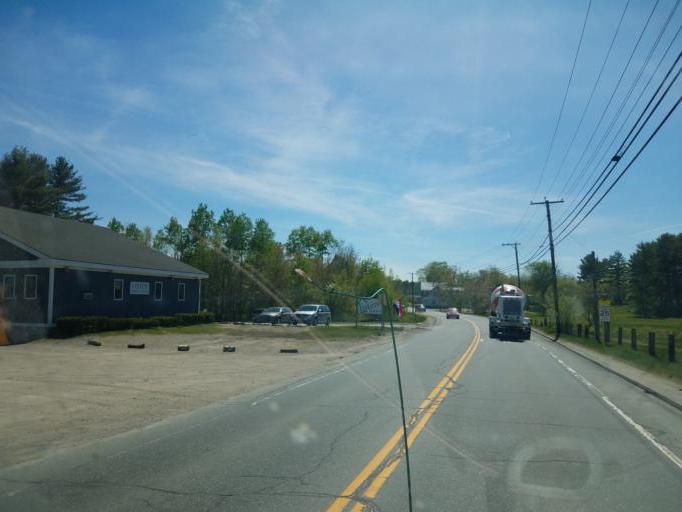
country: US
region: New Hampshire
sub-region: Grafton County
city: Enfield
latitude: 43.6508
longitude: -72.0947
